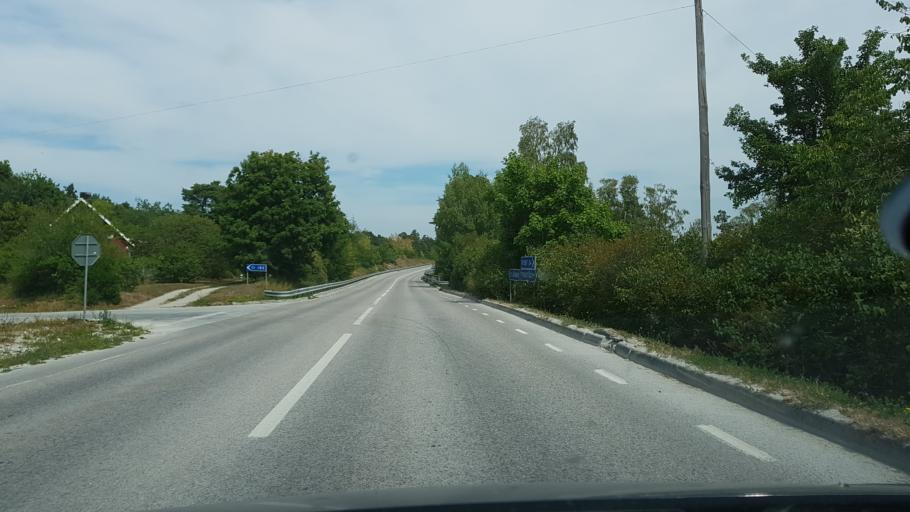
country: SE
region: Gotland
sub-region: Gotland
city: Slite
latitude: 57.7404
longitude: 18.6288
